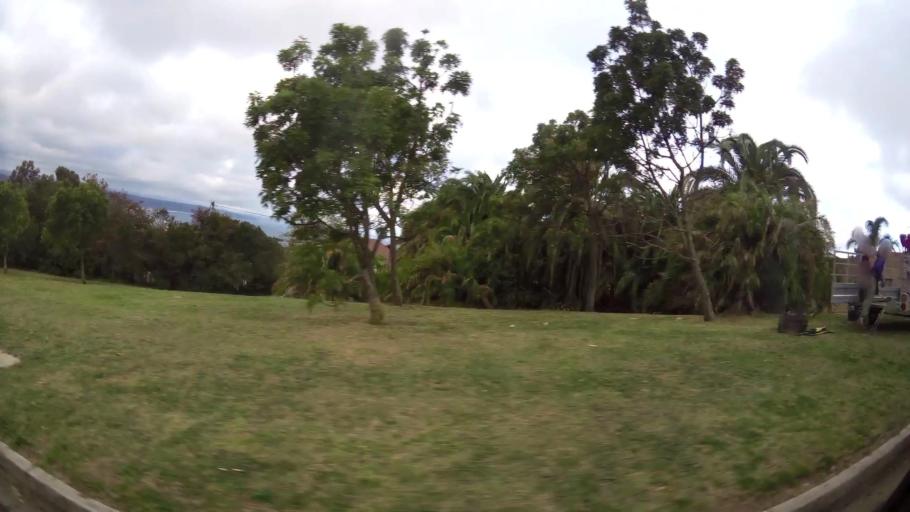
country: ZA
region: Western Cape
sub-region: Eden District Municipality
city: Plettenberg Bay
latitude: -34.0533
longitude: 23.3630
